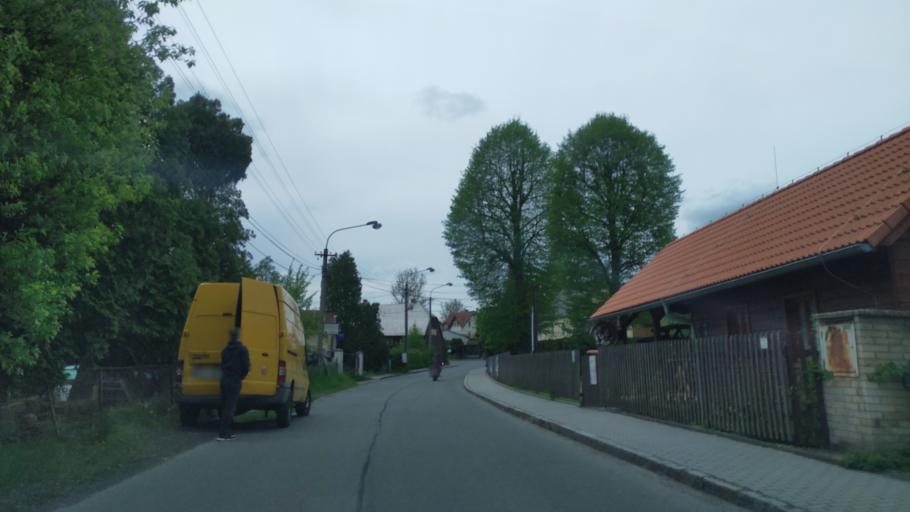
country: CZ
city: Novy Bor
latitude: 50.7451
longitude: 14.5924
